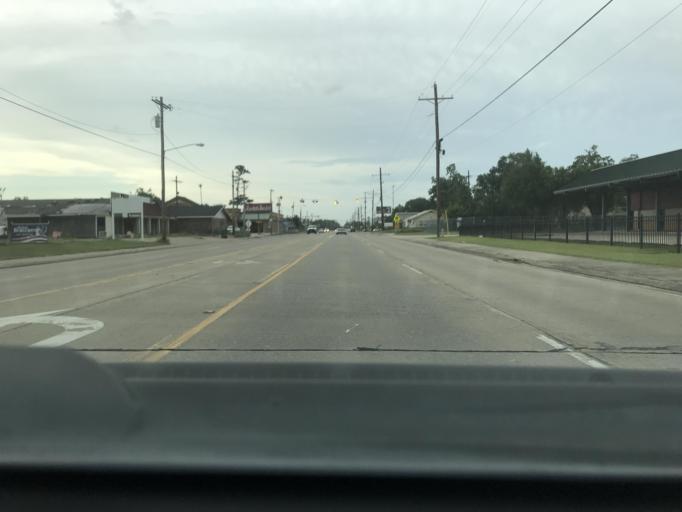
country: US
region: Louisiana
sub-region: Calcasieu Parish
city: Westlake
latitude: 30.2559
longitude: -93.2581
